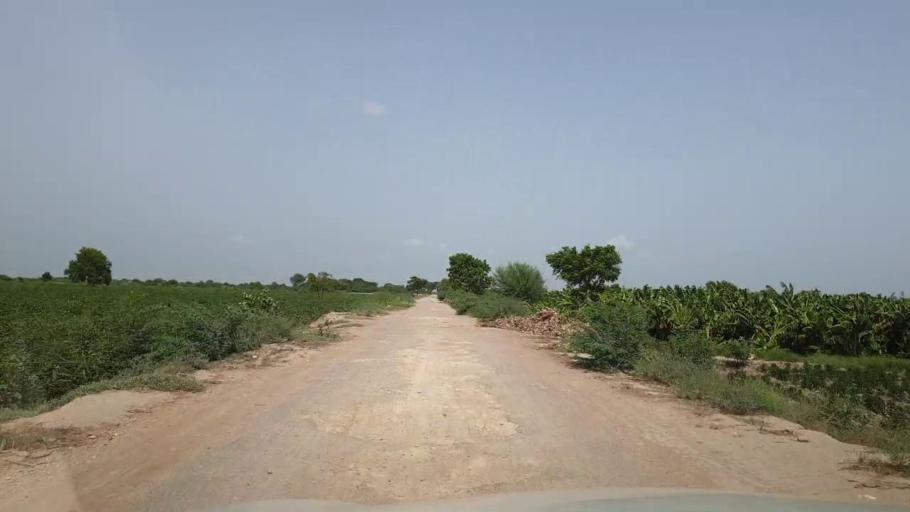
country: PK
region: Sindh
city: Mirwah Gorchani
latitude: 25.2561
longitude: 68.9419
